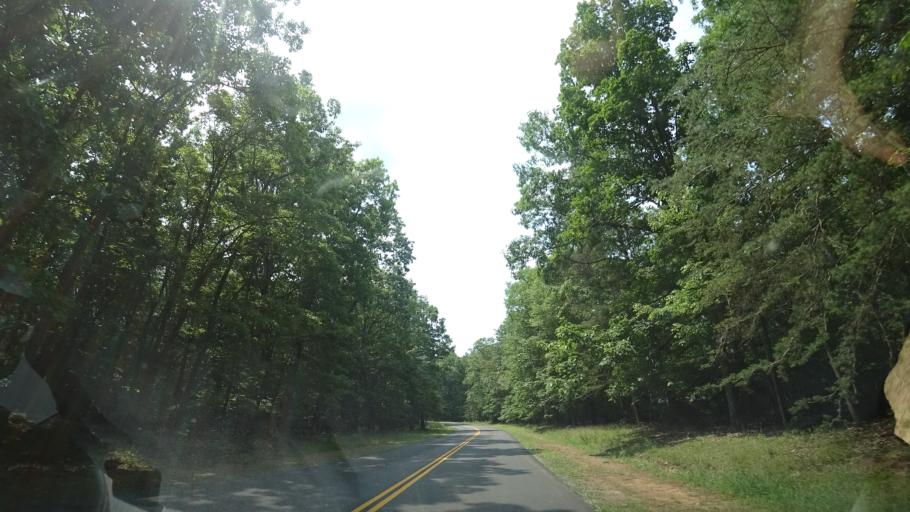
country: US
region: Virginia
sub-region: Louisa County
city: Louisa
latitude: 38.1217
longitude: -77.8232
